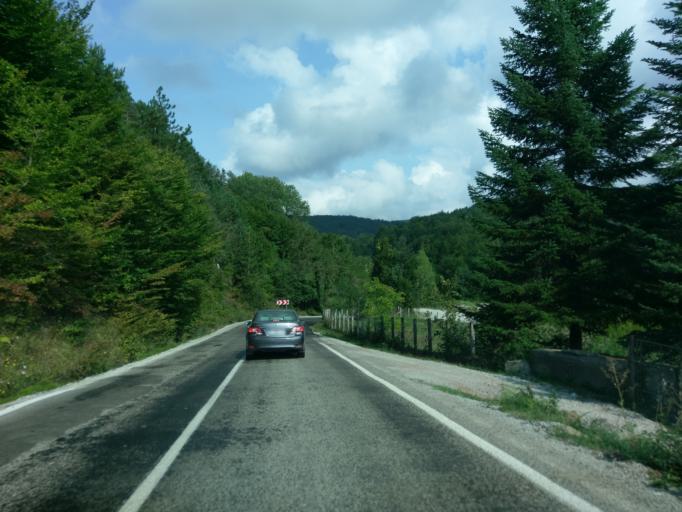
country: TR
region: Sinop
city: Ayancik
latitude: 41.8835
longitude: 34.5191
